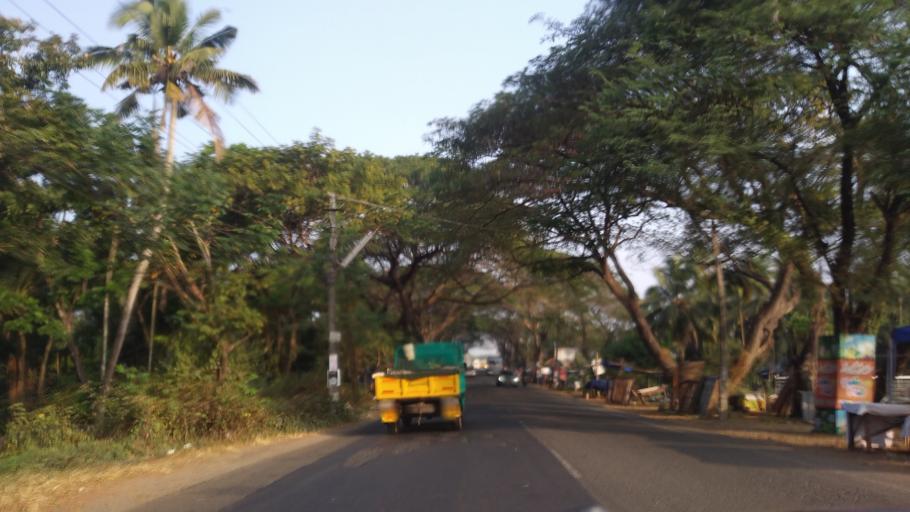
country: IN
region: Kerala
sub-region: Thrissur District
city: Kodungallur
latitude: 10.1964
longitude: 76.2009
